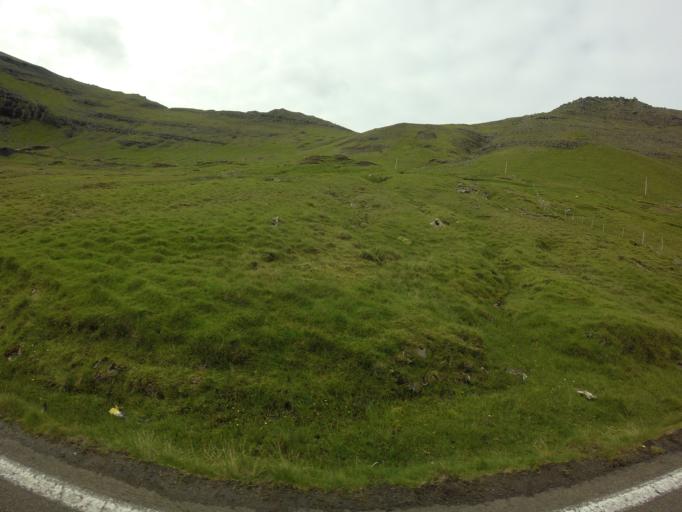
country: FO
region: Suduroy
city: Tvoroyri
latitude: 61.5734
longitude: -6.9353
